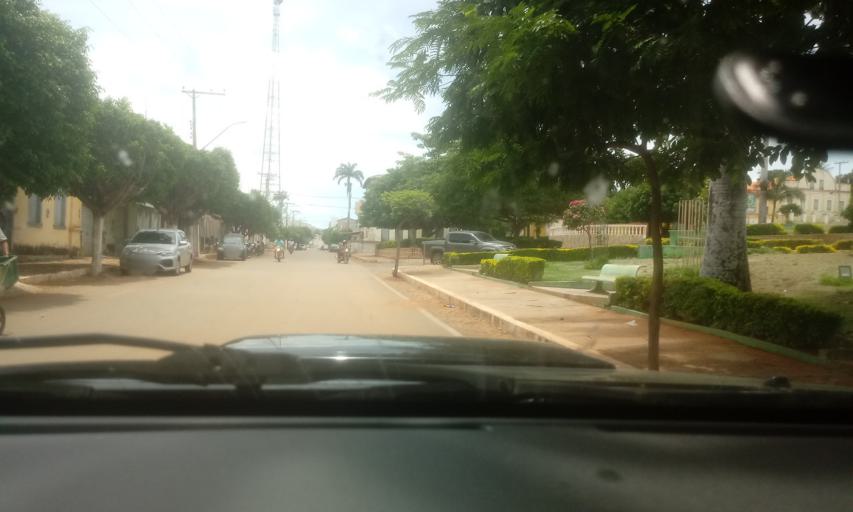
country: BR
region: Bahia
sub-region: Riacho De Santana
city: Riacho de Santana
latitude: -13.6089
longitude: -42.9410
